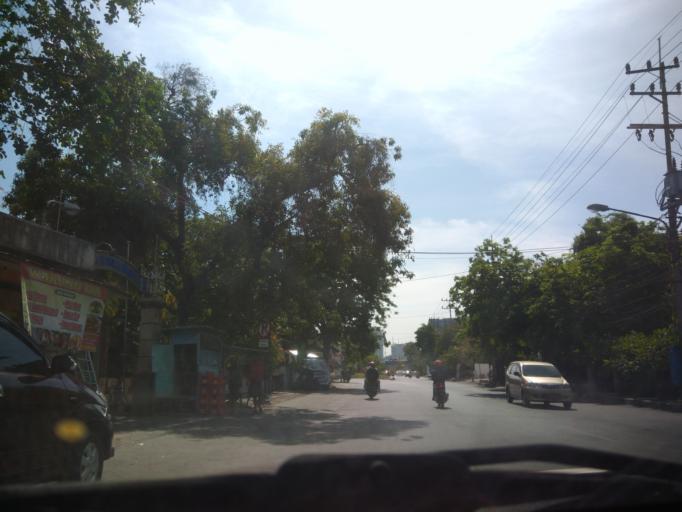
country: ID
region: East Java
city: Gubengairlangga
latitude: -7.2659
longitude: 112.7624
